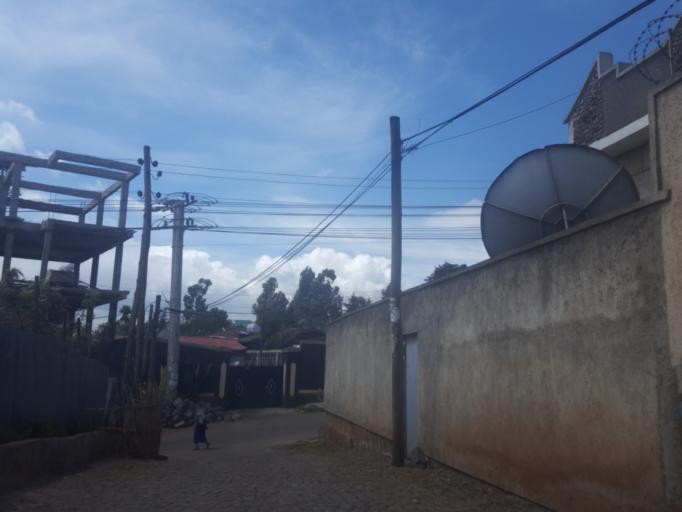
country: ET
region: Adis Abeba
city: Addis Ababa
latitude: 9.0643
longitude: 38.7427
